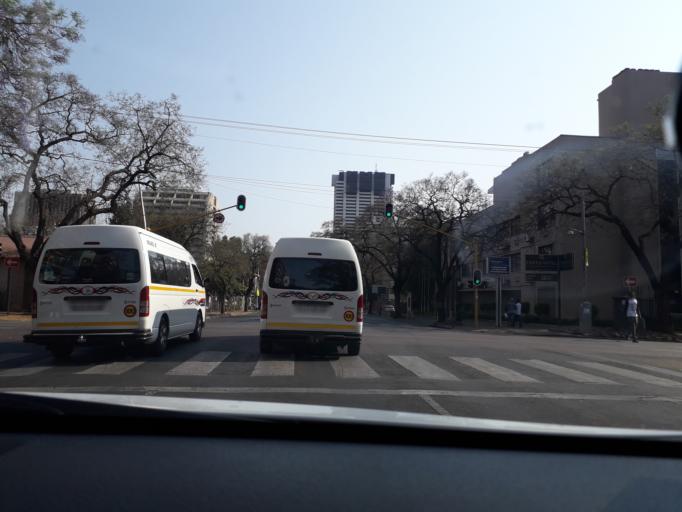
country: ZA
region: Gauteng
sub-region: City of Tshwane Metropolitan Municipality
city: Pretoria
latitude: -25.7522
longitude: 28.1935
